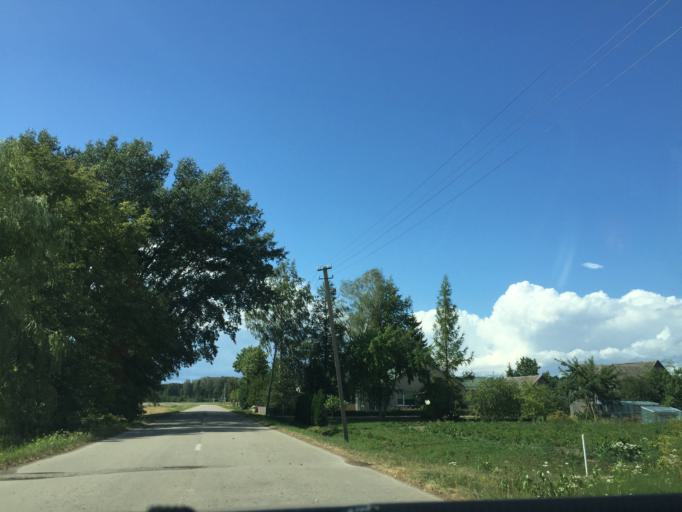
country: LT
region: Siauliu apskritis
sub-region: Joniskis
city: Joniskis
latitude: 56.3303
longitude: 23.5669
